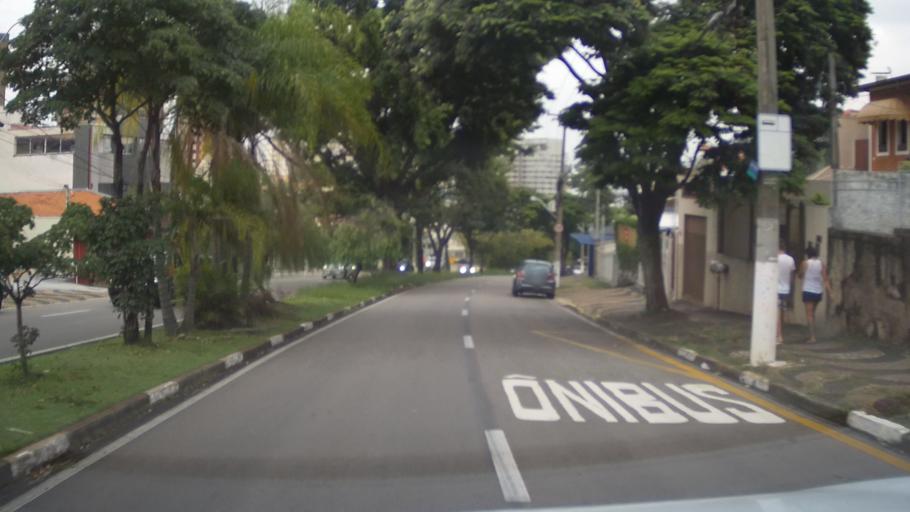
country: BR
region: Sao Paulo
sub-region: Campinas
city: Campinas
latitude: -22.9131
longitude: -47.0479
